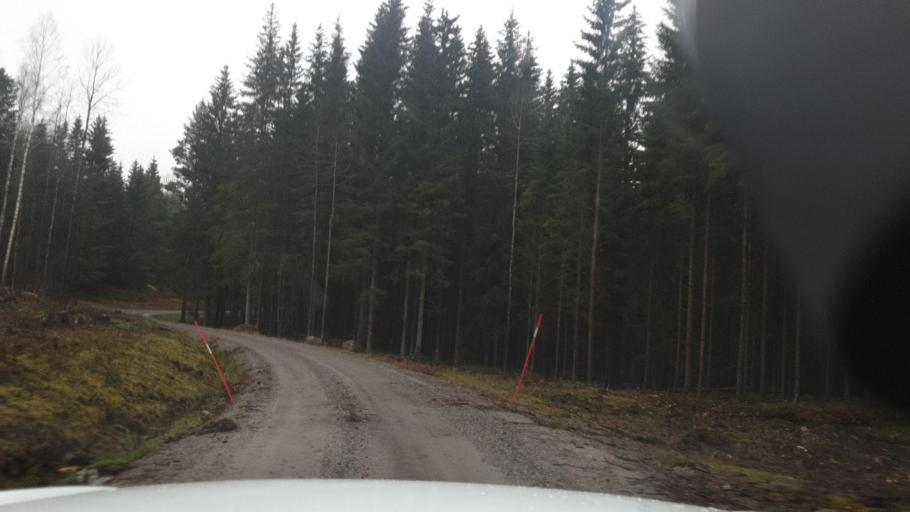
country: SE
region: Vaermland
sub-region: Arvika Kommun
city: Arvika
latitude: 59.5808
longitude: 12.8214
